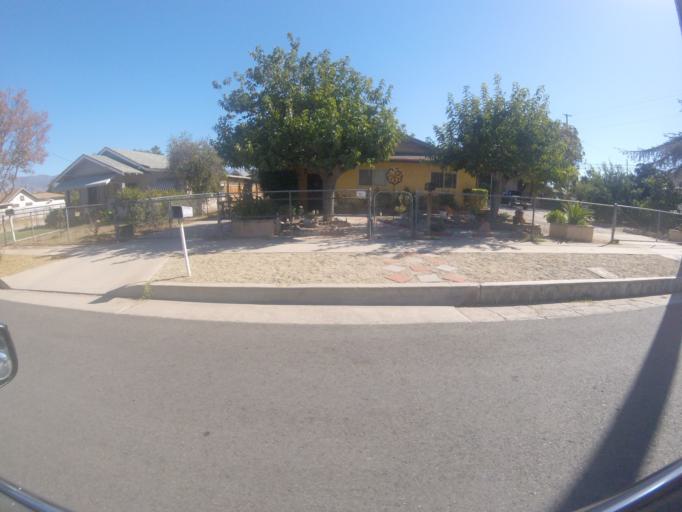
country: US
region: California
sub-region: San Bernardino County
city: Redlands
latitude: 34.0668
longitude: -117.1858
